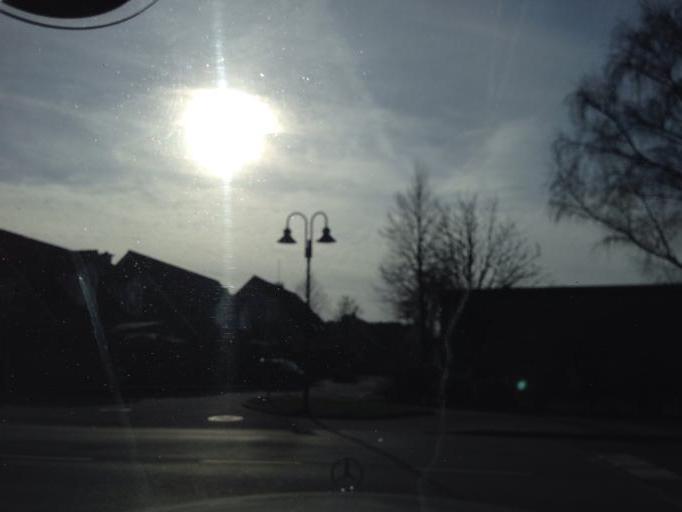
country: DE
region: Lower Saxony
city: Hasbergen
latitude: 52.2090
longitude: 7.9210
